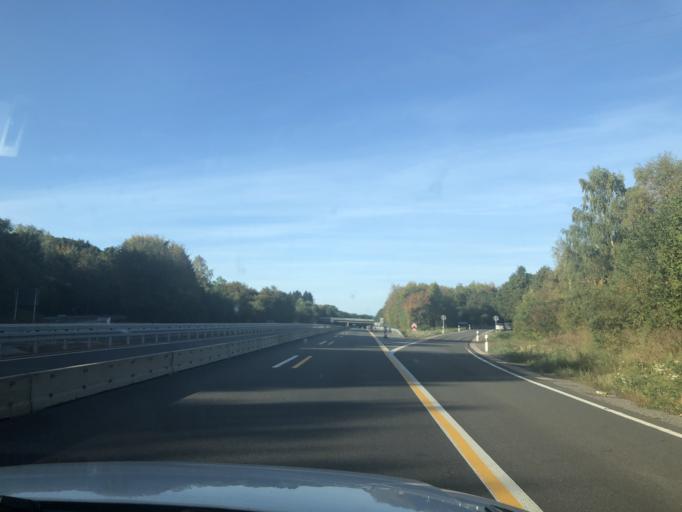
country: DE
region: Saarland
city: Tholey
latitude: 49.5036
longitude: 6.9925
